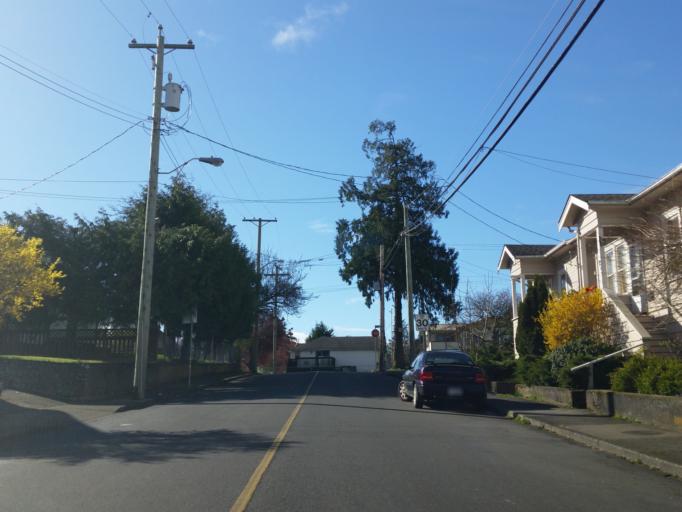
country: CA
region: British Columbia
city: Victoria
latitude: 48.4335
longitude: -123.3938
